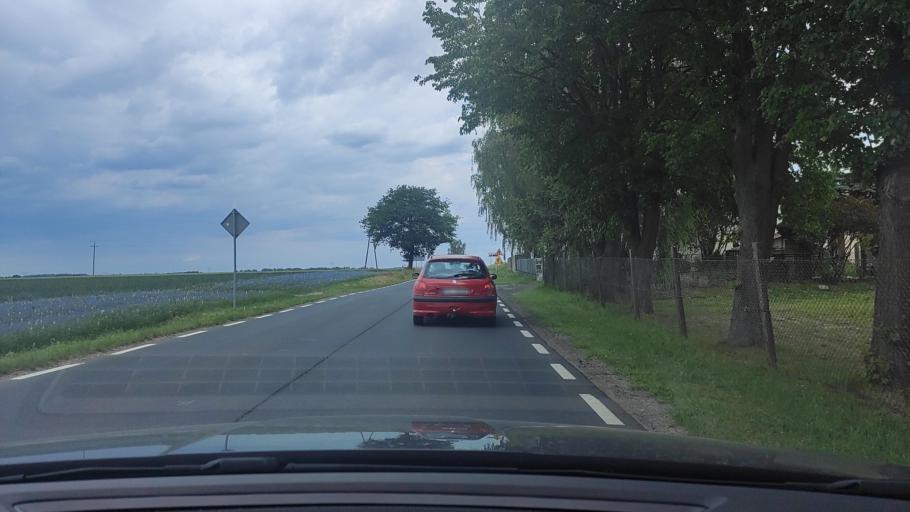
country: PL
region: Greater Poland Voivodeship
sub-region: Powiat poznanski
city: Swarzedz
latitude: 52.4278
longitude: 17.1579
